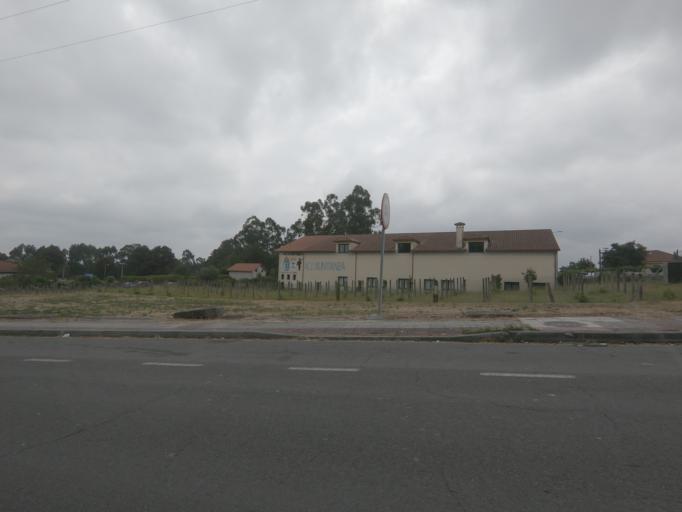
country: ES
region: Galicia
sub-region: Provincia de Pontevedra
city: Tui
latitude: 42.0503
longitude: -8.6582
